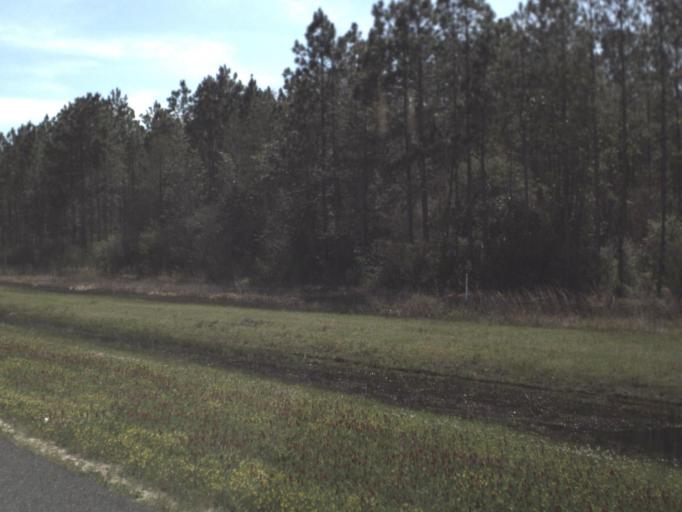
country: US
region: Florida
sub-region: Bay County
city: Lynn Haven
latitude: 30.3418
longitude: -85.6611
